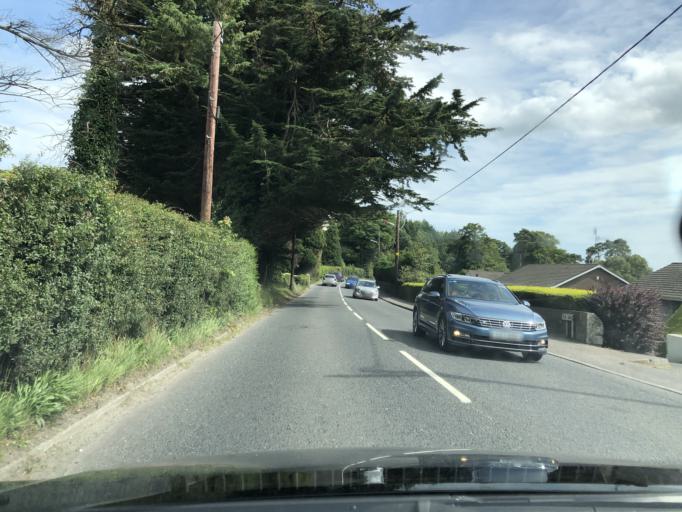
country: GB
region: Northern Ireland
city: Ballynahinch
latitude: 54.3976
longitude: -5.8927
